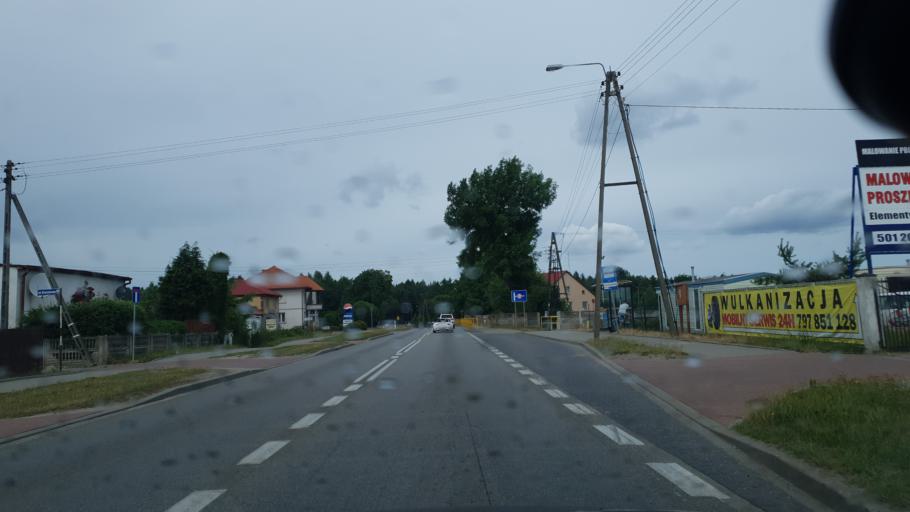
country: PL
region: Pomeranian Voivodeship
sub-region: Powiat kartuski
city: Chwaszczyno
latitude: 54.4285
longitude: 18.3890
